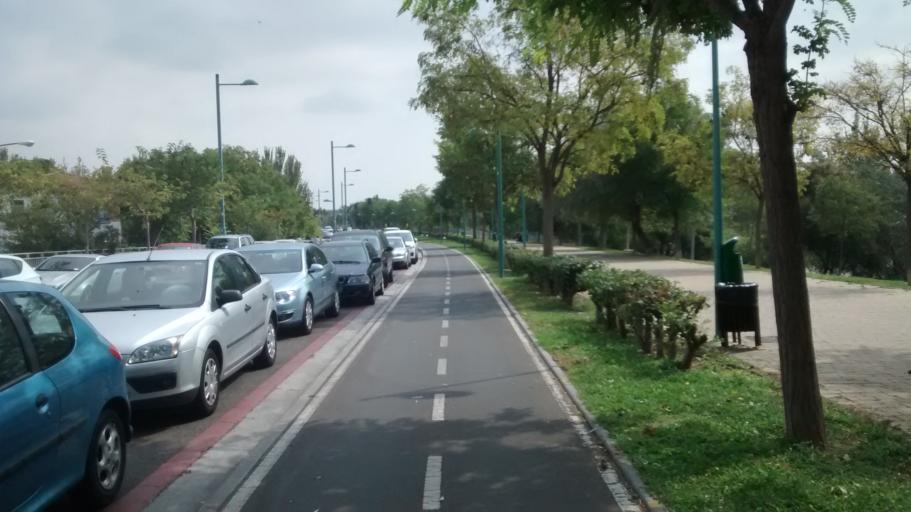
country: ES
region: Aragon
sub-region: Provincia de Zaragoza
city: Zaragoza
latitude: 41.6556
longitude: -0.8676
